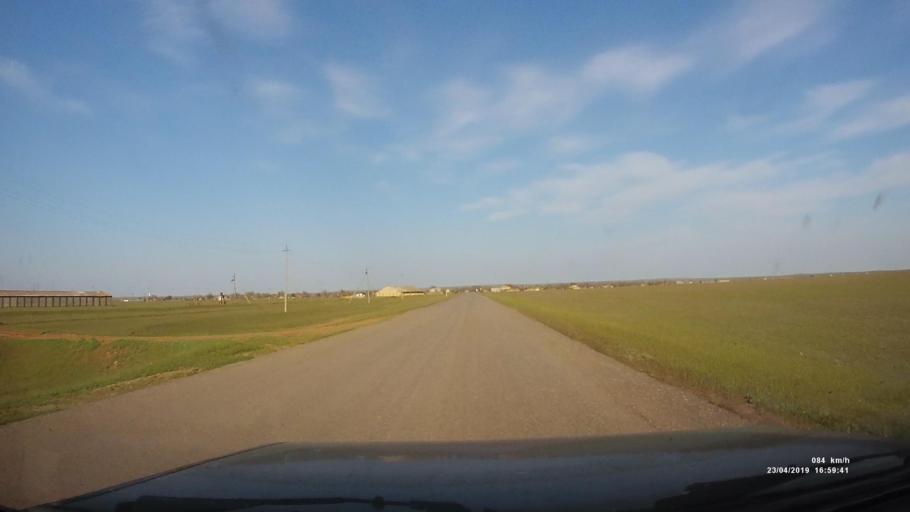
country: RU
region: Kalmykiya
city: Priyutnoye
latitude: 46.3087
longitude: 43.3941
